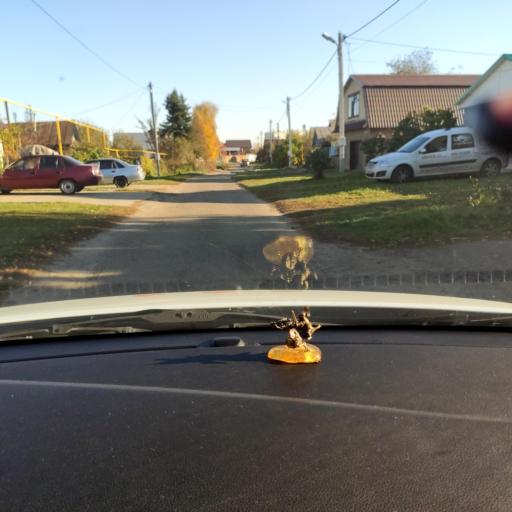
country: RU
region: Tatarstan
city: Stolbishchi
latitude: 55.6242
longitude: 49.1537
